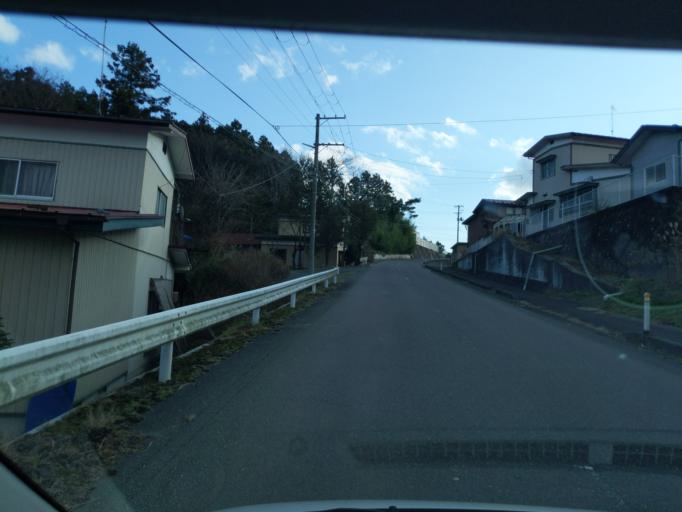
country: JP
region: Miyagi
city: Wakuya
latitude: 38.7014
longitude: 141.1579
